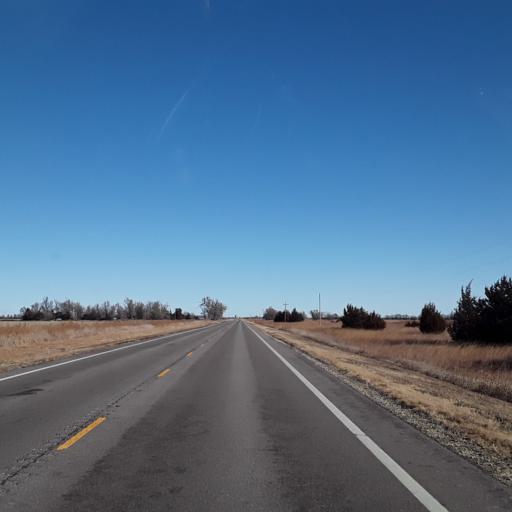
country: US
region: Kansas
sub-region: Pawnee County
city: Larned
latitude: 38.1214
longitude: -99.1772
